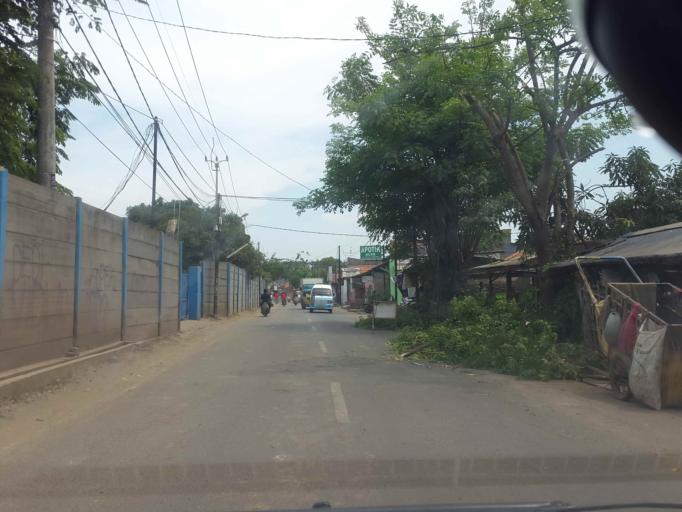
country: ID
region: Banten
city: Tangerang
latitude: -6.1534
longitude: 106.6249
